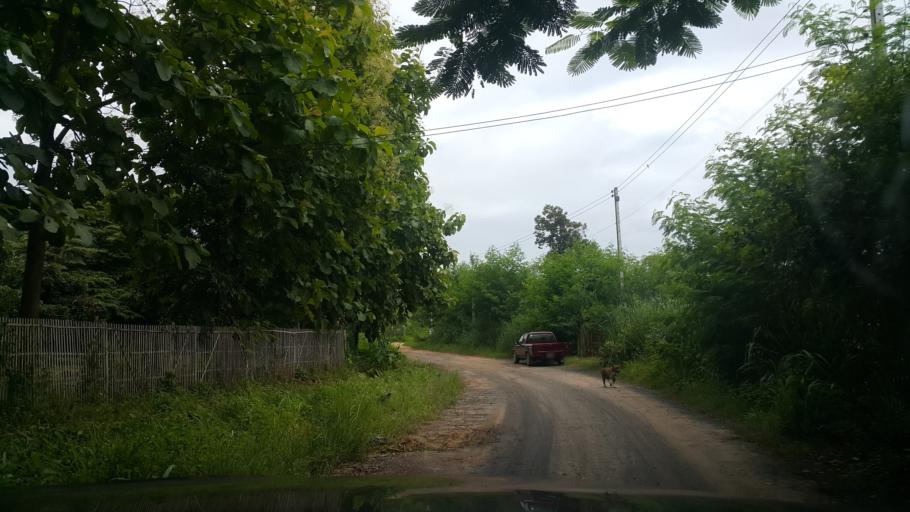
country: TH
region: Chiang Mai
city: San Sai
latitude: 18.9107
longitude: 99.0589
